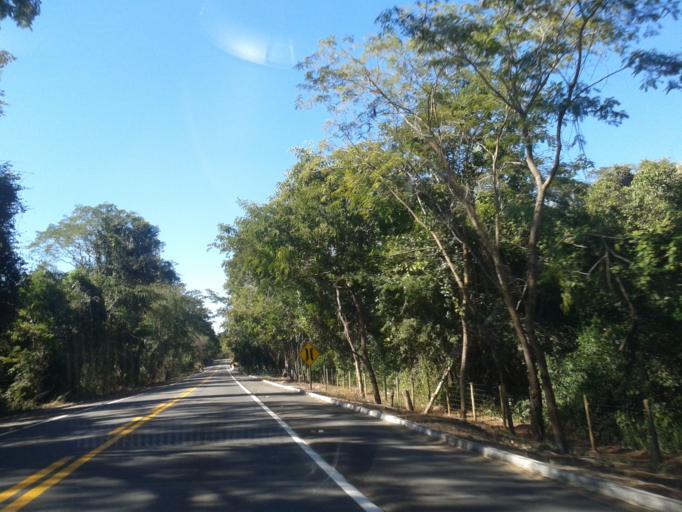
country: BR
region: Goias
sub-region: Goias
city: Goias
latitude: -15.9046
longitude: -50.1166
